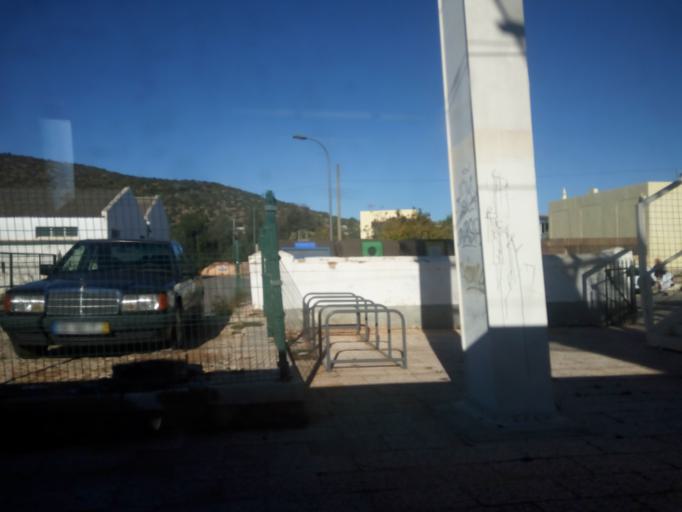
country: PT
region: Faro
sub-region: Loule
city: Almancil
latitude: 37.1044
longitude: -8.0585
